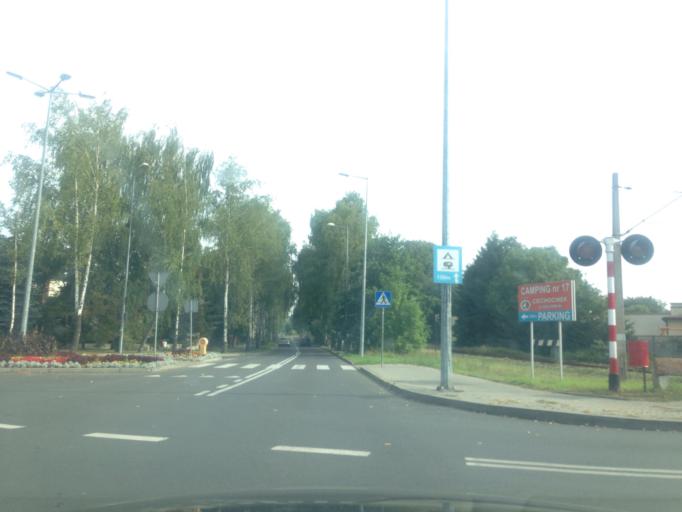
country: PL
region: Kujawsko-Pomorskie
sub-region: Powiat aleksandrowski
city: Ciechocinek
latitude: 52.8787
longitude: 18.7790
